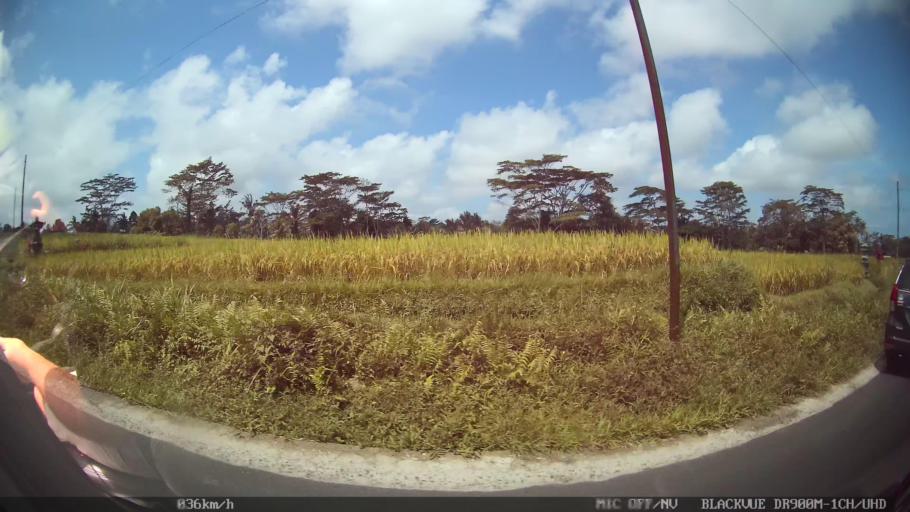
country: ID
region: Bali
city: Banjar Apuan Kaja
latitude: -8.4941
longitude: 115.3415
